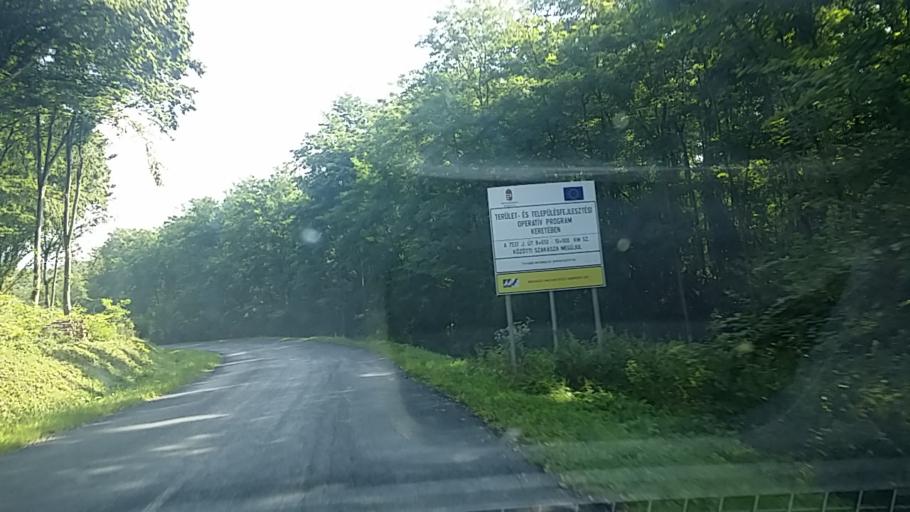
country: HU
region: Zala
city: Letenye
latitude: 46.5275
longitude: 16.7105
